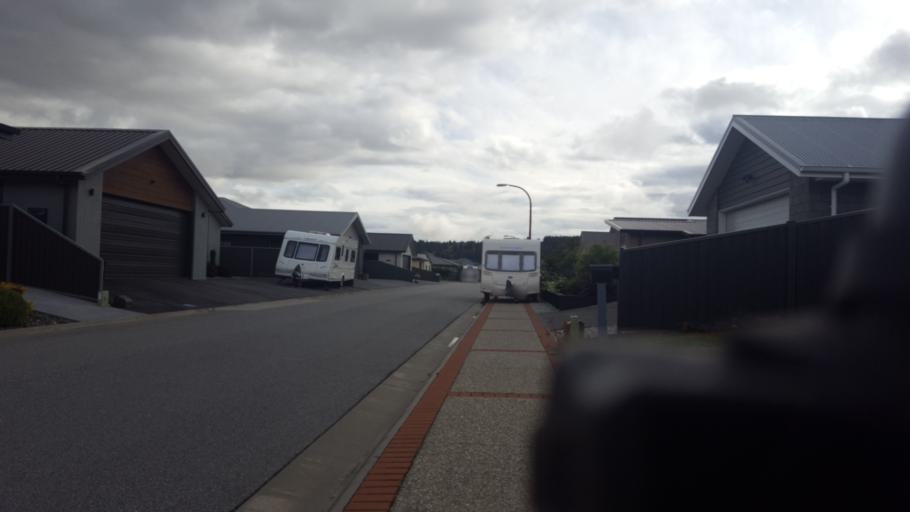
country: NZ
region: Otago
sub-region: Queenstown-Lakes District
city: Wanaka
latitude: -45.2414
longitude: 169.3786
